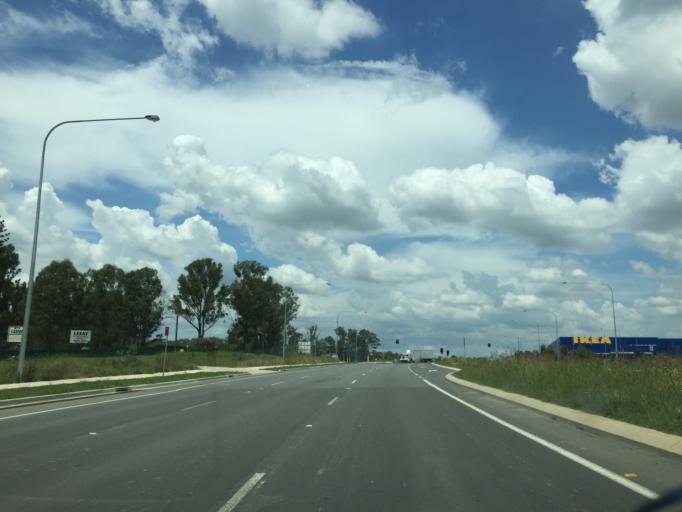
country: AU
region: New South Wales
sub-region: Blacktown
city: Hassall Grove
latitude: -33.7158
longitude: 150.8438
